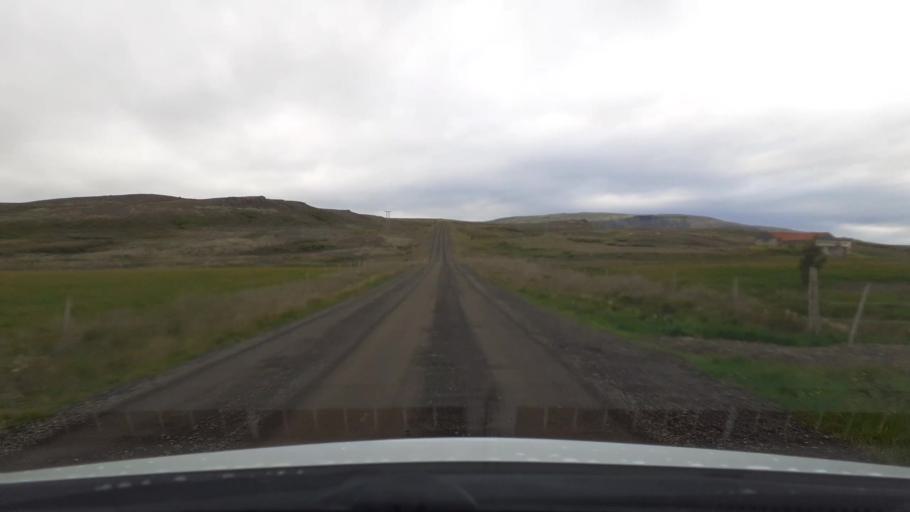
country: IS
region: Capital Region
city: Mosfellsbaer
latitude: 64.2021
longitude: -21.5598
